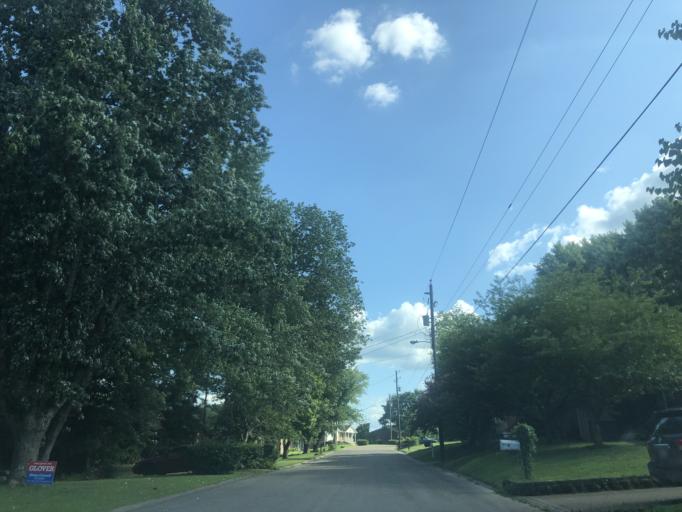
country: US
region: Tennessee
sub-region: Wilson County
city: Green Hill
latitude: 36.2082
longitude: -86.5925
